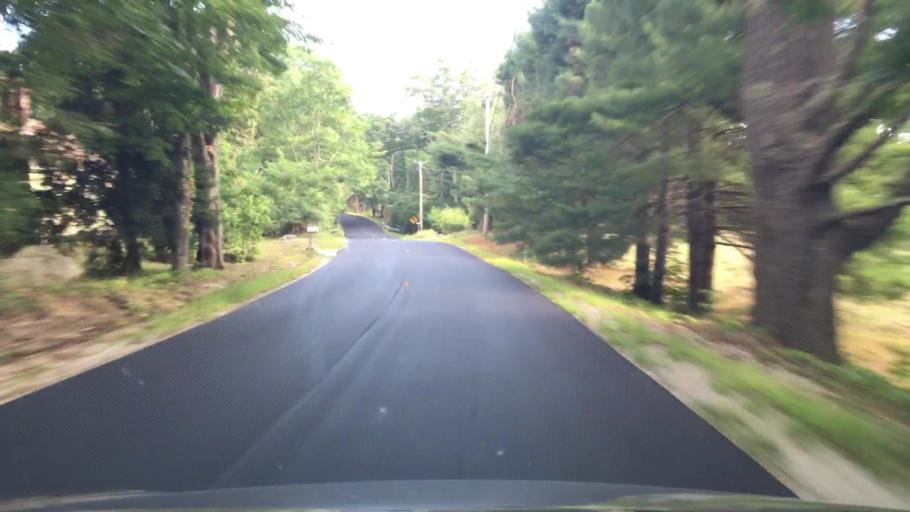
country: US
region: Maine
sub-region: Hancock County
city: Surry
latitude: 44.5189
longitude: -68.6076
